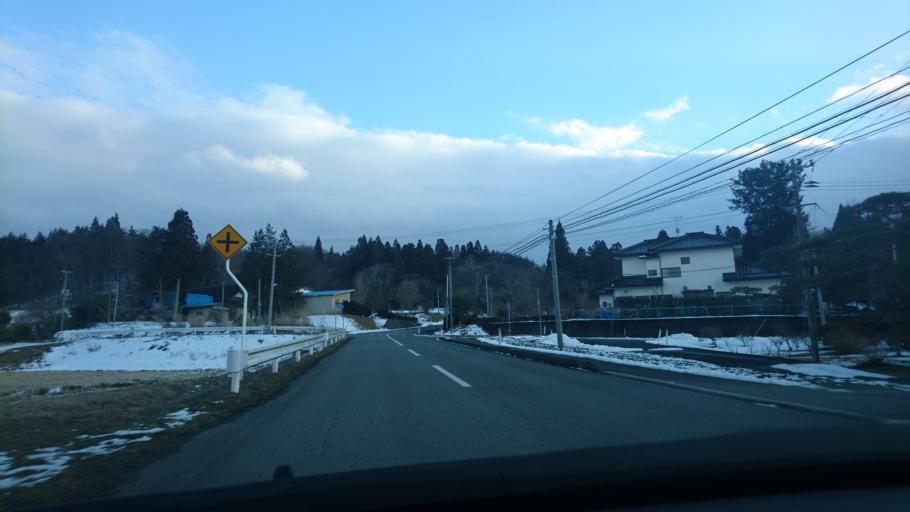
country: JP
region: Iwate
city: Ichinoseki
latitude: 39.0162
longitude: 141.3390
